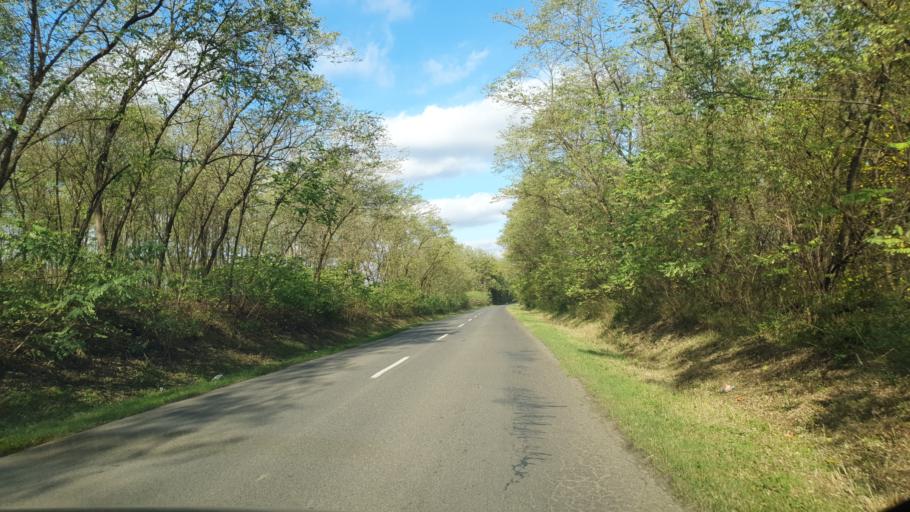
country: HU
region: Szabolcs-Szatmar-Bereg
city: Anarcs
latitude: 48.1540
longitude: 22.0940
